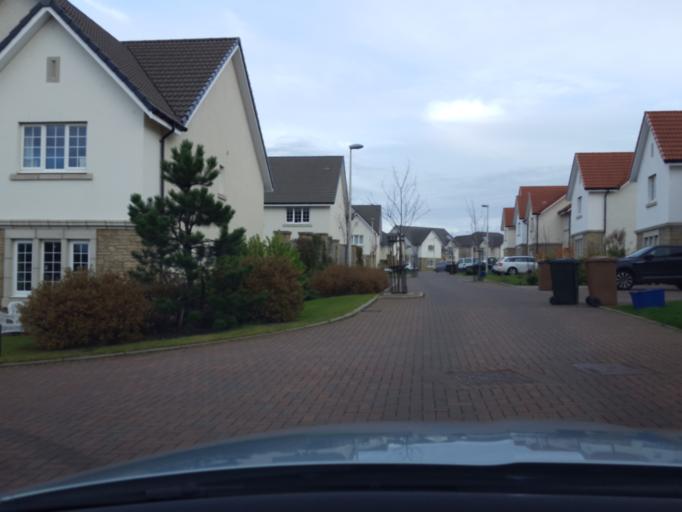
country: GB
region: Scotland
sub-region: Edinburgh
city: Ratho
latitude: 55.9256
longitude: -3.3744
